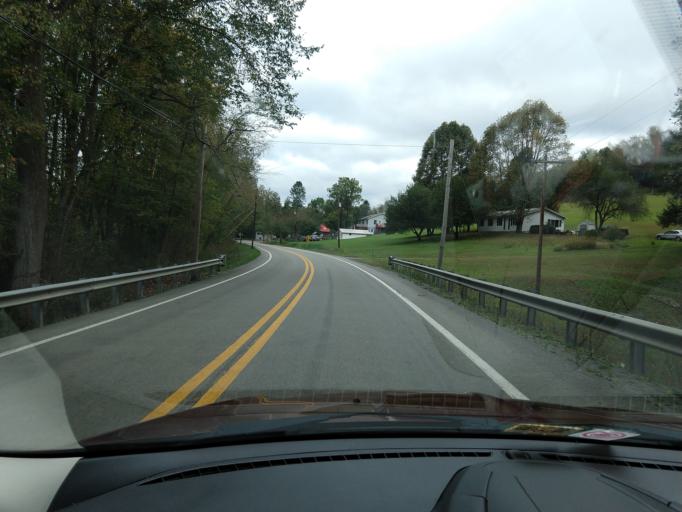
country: US
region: West Virginia
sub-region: Barbour County
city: Belington
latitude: 39.0030
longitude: -79.9377
